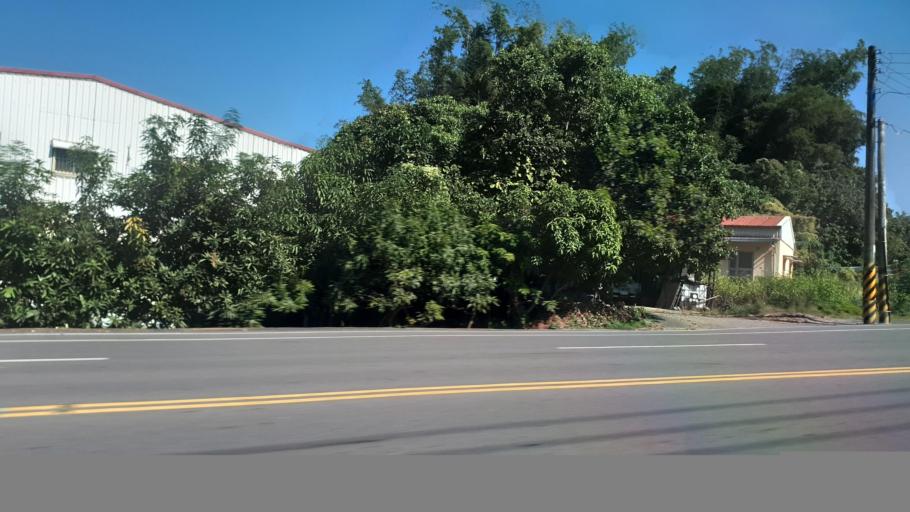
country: TW
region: Taiwan
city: Yujing
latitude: 23.0647
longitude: 120.3833
